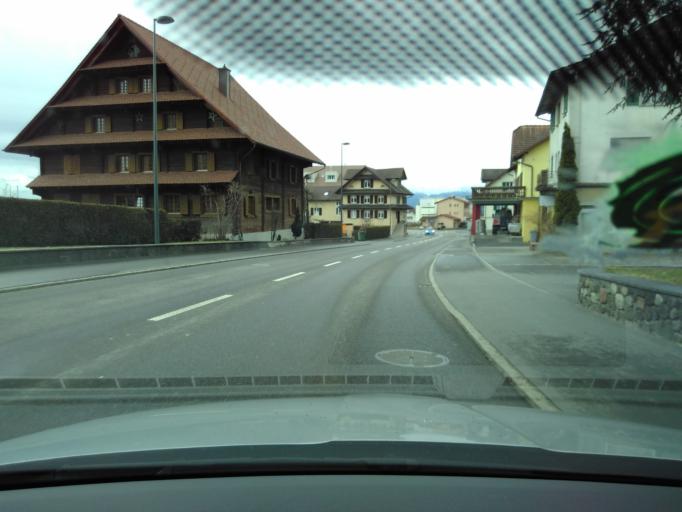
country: CH
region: Lucerne
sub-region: Sursee District
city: Hildisrieden
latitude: 47.1504
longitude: 8.2293
